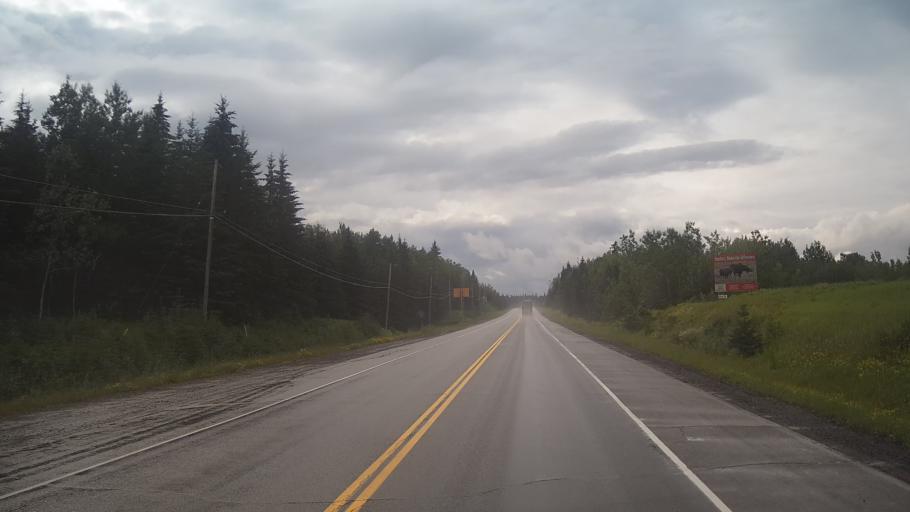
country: CA
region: Ontario
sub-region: Thunder Bay District
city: Thunder Bay
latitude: 48.5414
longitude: -89.6642
